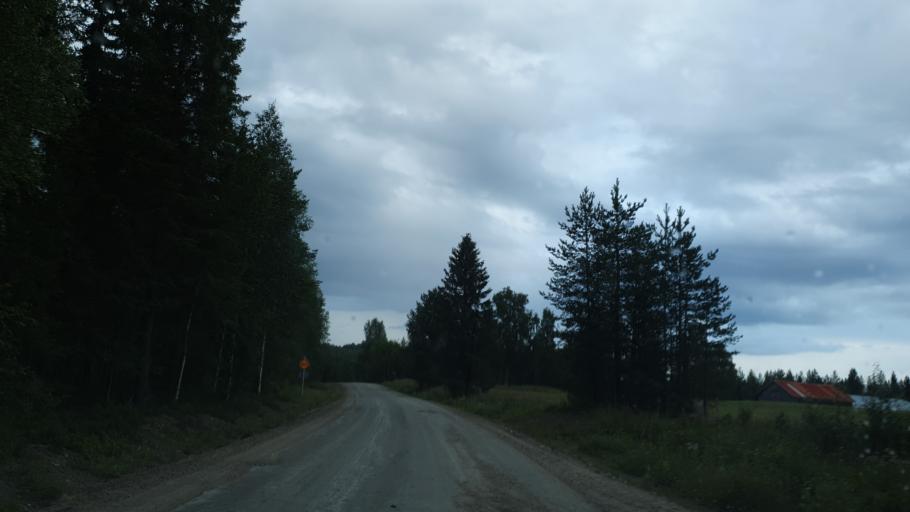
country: FI
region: Kainuu
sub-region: Kehys-Kainuu
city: Kuhmo
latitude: 64.2066
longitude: 29.3714
